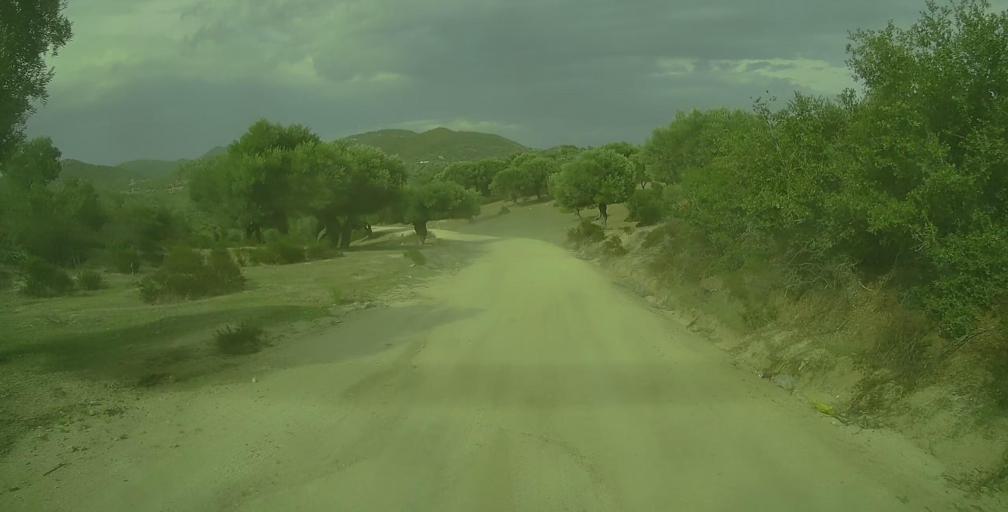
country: GR
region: Central Macedonia
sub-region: Nomos Chalkidikis
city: Sykia
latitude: 40.0026
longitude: 23.9244
